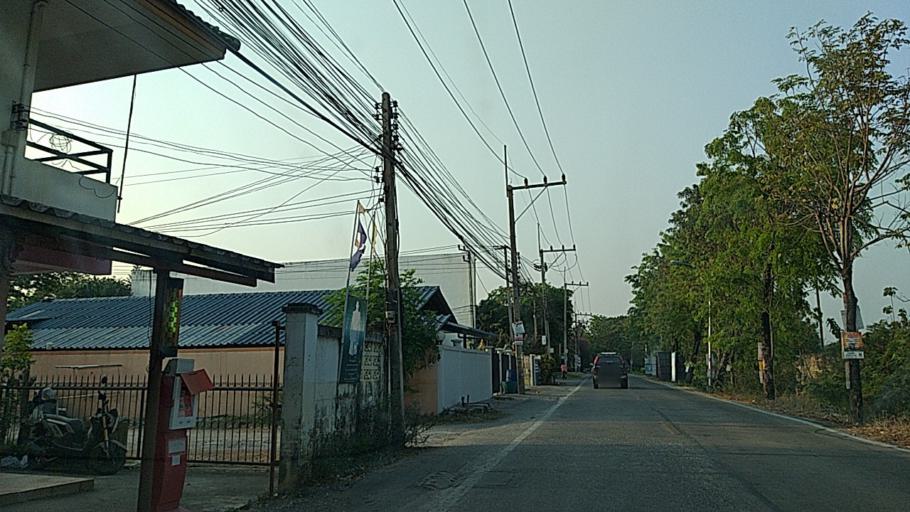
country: TH
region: Phra Nakhon Si Ayutthaya
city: Ban Bang Kadi Pathum Thani
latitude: 13.9976
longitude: 100.5643
